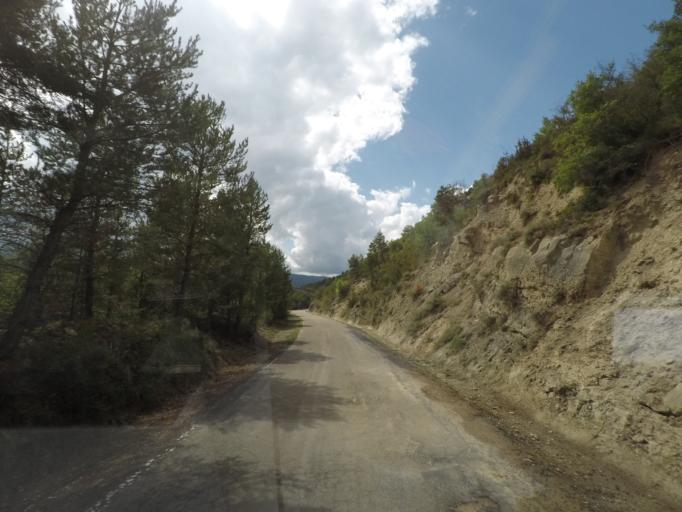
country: ES
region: Aragon
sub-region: Provincia de Huesca
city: Yebra de Basa
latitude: 42.3962
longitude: -0.2655
